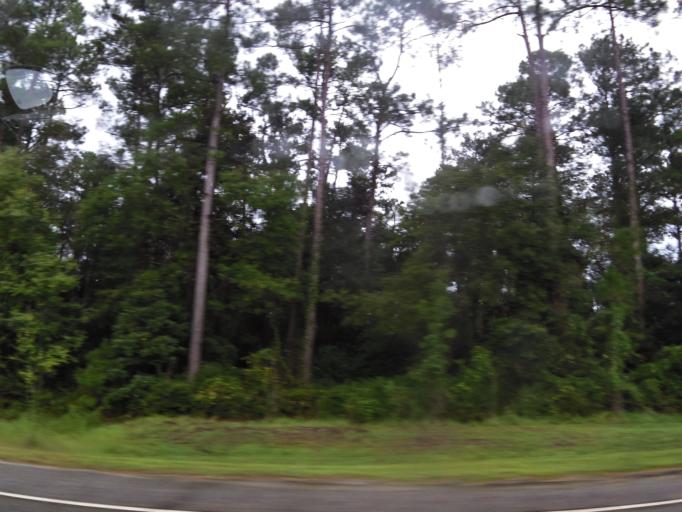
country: US
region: Georgia
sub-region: Wayne County
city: Jesup
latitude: 31.5555
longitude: -81.8212
